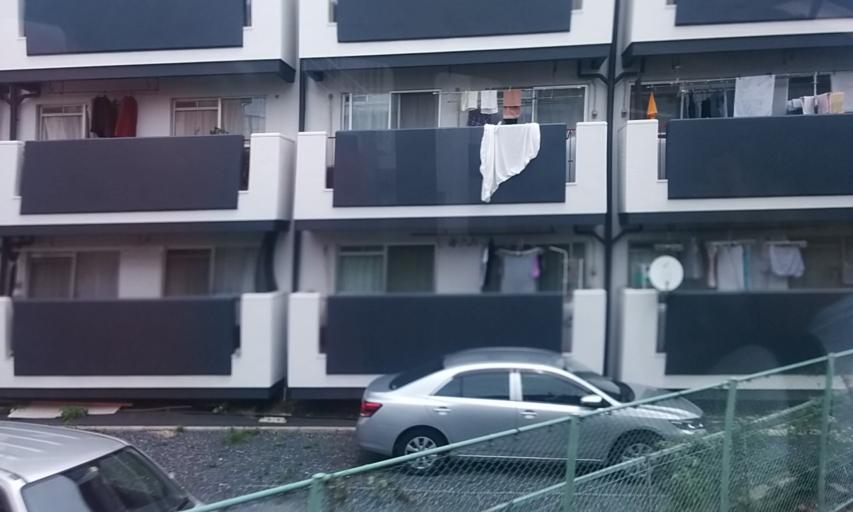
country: JP
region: Osaka
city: Ikeda
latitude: 34.8109
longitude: 135.4496
